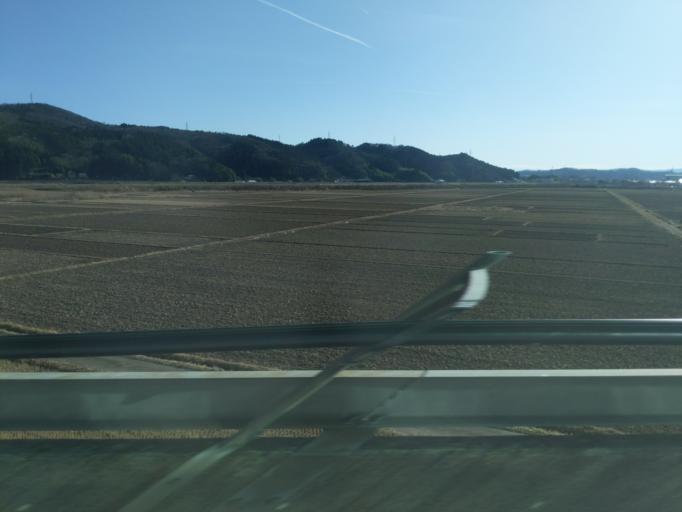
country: JP
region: Miyagi
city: Okawara
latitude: 38.0778
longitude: 140.7364
